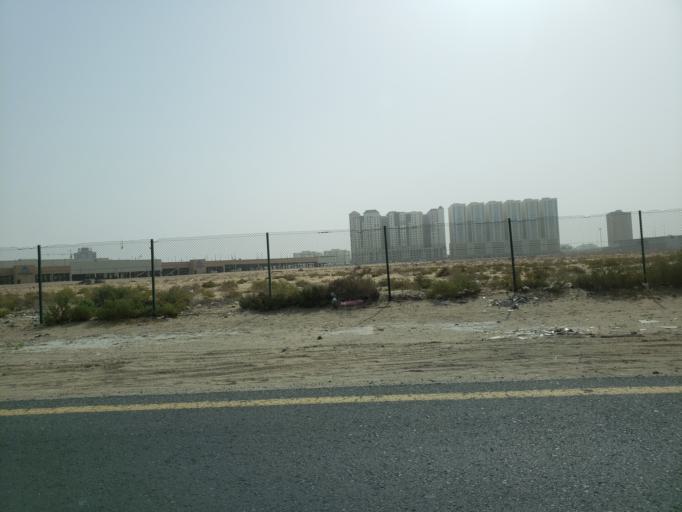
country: AE
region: Ajman
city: Ajman
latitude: 25.3955
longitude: 55.4756
